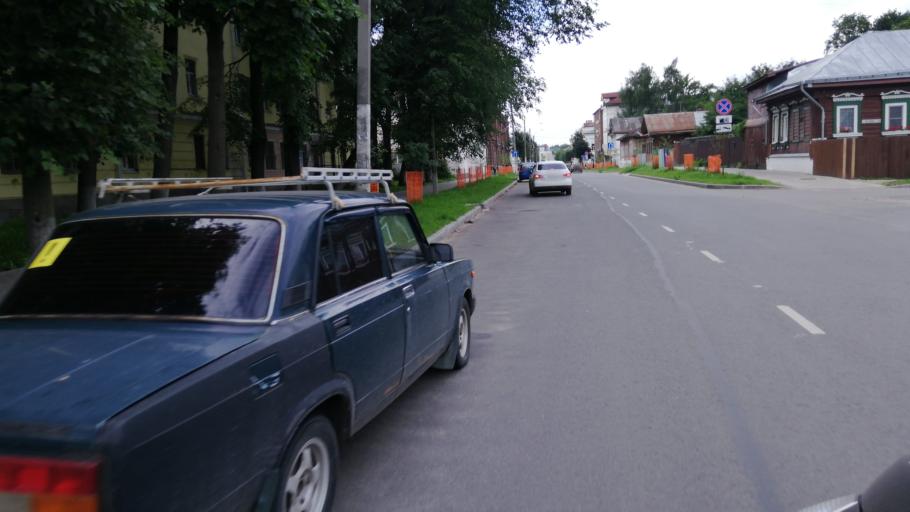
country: RU
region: Kostroma
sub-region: Kostromskoy Rayon
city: Kostroma
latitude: 57.7695
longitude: 40.9352
